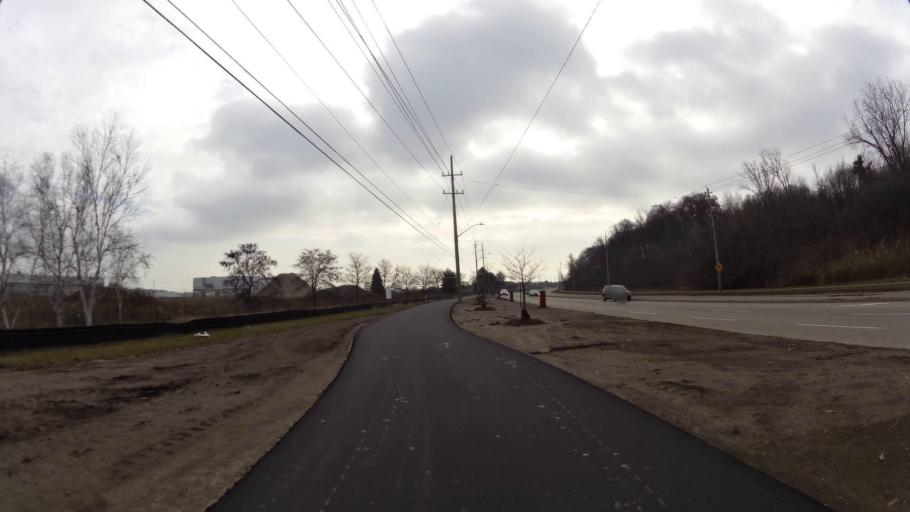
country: CA
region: Ontario
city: Kitchener
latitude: 43.4093
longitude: -80.4600
